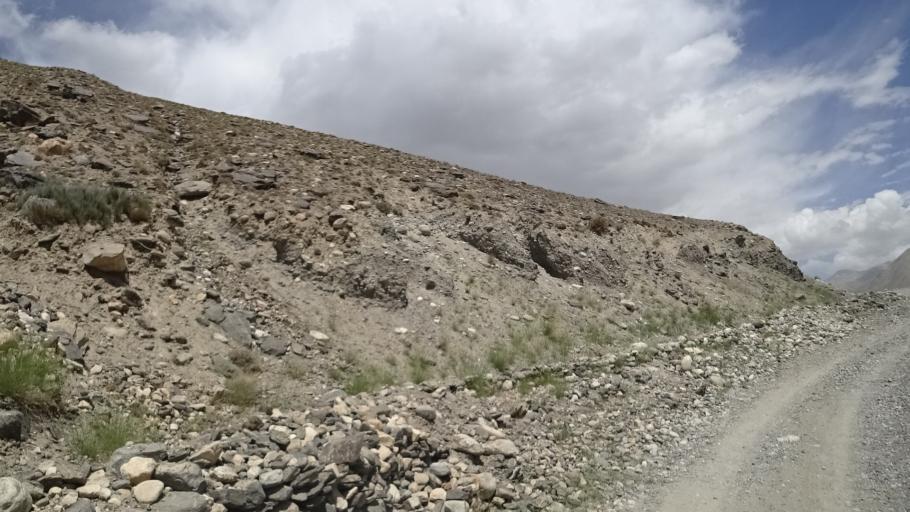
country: AF
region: Badakhshan
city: Khandud
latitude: 37.0855
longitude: 72.7007
